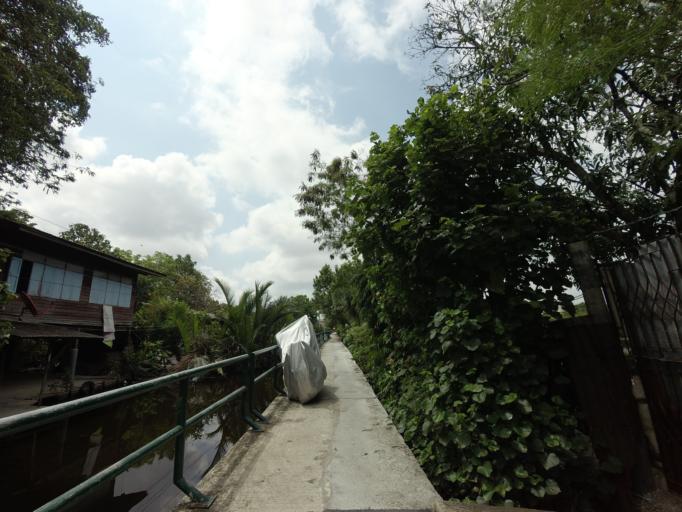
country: TH
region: Bangkok
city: Thung Khru
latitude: 13.6345
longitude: 100.4937
